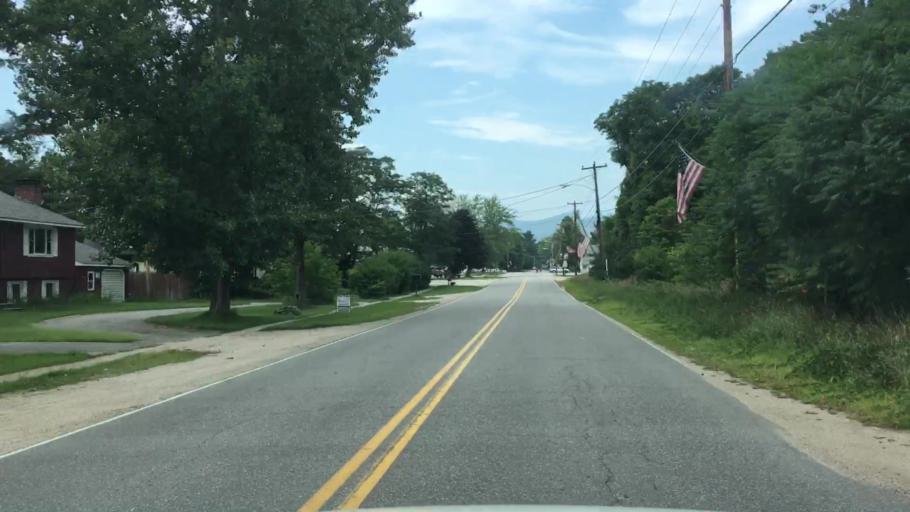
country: US
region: Maine
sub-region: Oxford County
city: Rumford
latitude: 44.6327
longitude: -70.7494
